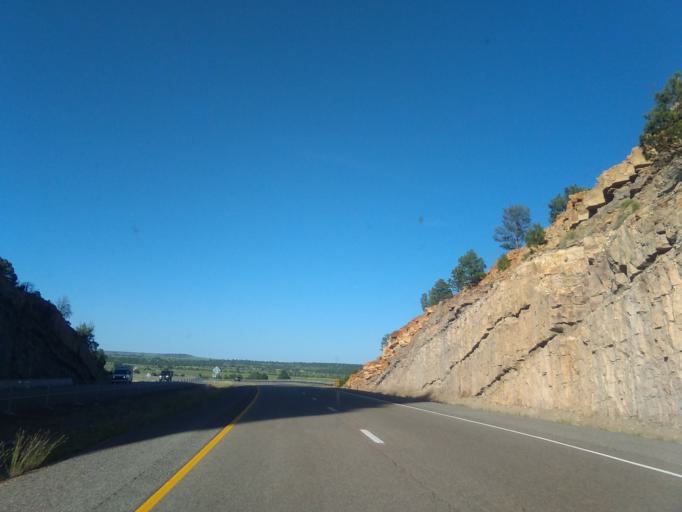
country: US
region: New Mexico
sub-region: San Miguel County
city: Las Vegas
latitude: 35.5260
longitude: -105.2381
